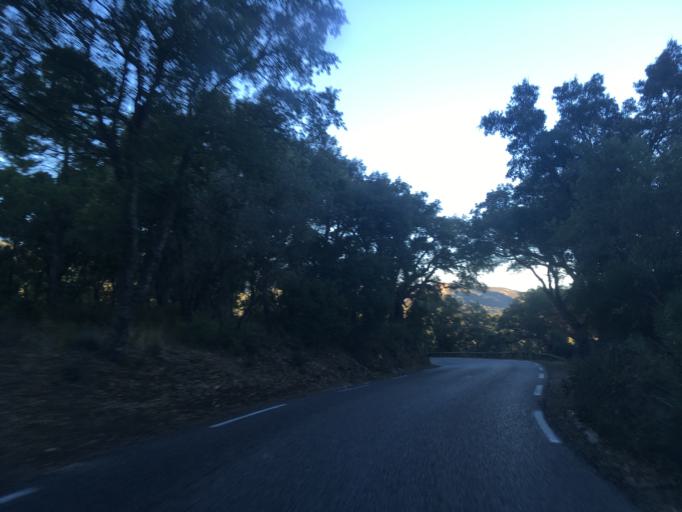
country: FR
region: Provence-Alpes-Cote d'Azur
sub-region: Departement du Var
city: Le Plan-de-la-Tour
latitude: 43.3153
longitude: 6.5432
